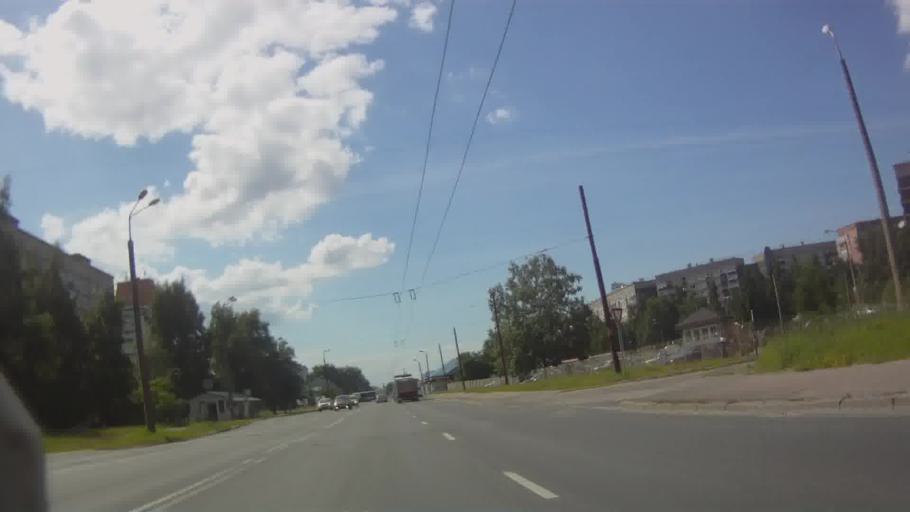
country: LV
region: Stopini
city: Ulbroka
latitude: 56.9475
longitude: 24.1995
